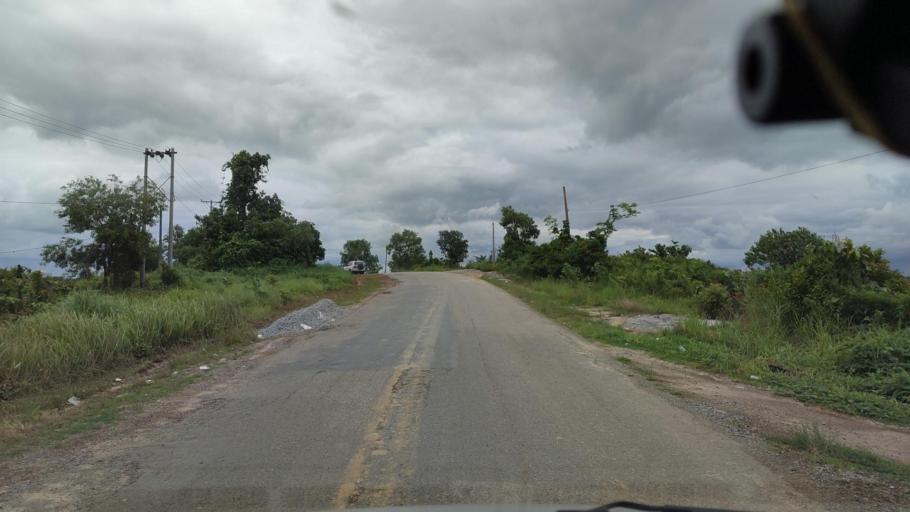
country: MM
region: Bago
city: Bago
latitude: 17.2526
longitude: 96.4315
